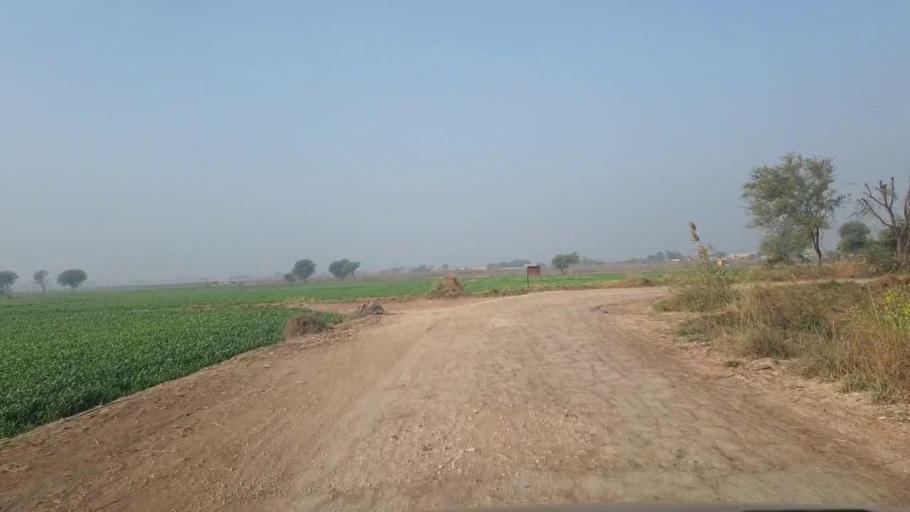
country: PK
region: Sindh
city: Shahdadpur
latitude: 25.9444
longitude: 68.5868
